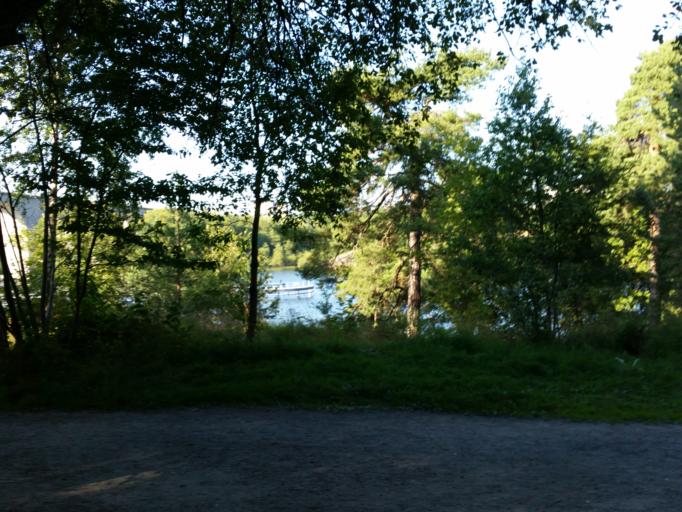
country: SE
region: Stockholm
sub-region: Stockholms Kommun
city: Arsta
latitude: 59.3048
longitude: 18.0413
